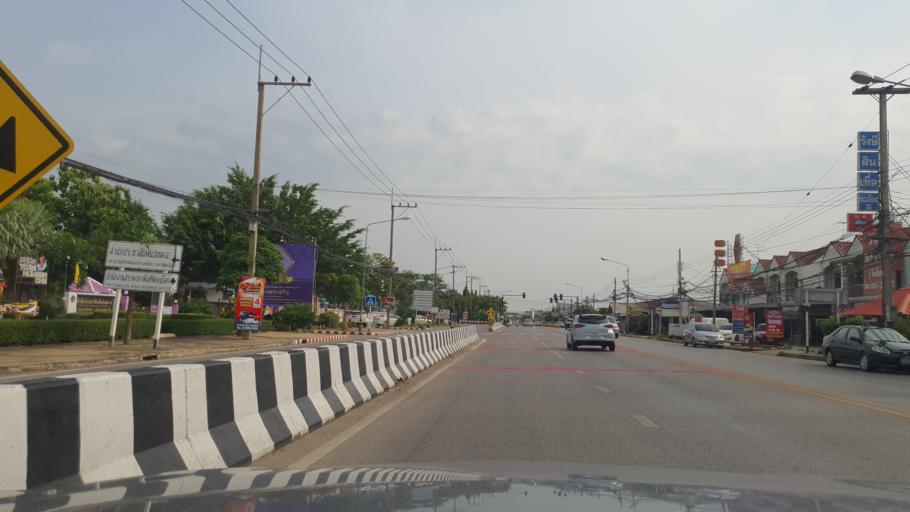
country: TH
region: Phitsanulok
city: Phitsanulok
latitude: 16.8410
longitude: 100.2657
